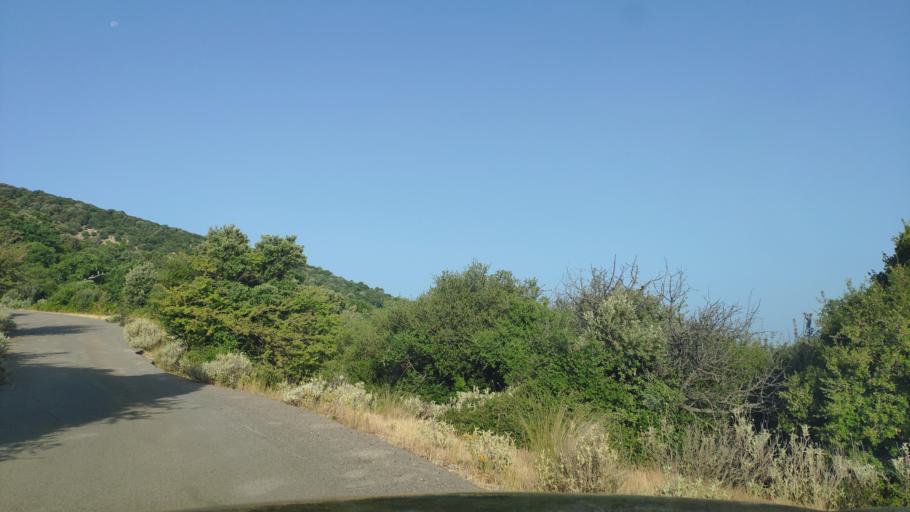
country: GR
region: West Greece
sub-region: Nomos Aitolias kai Akarnanias
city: Monastirakion
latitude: 38.8420
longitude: 20.9717
